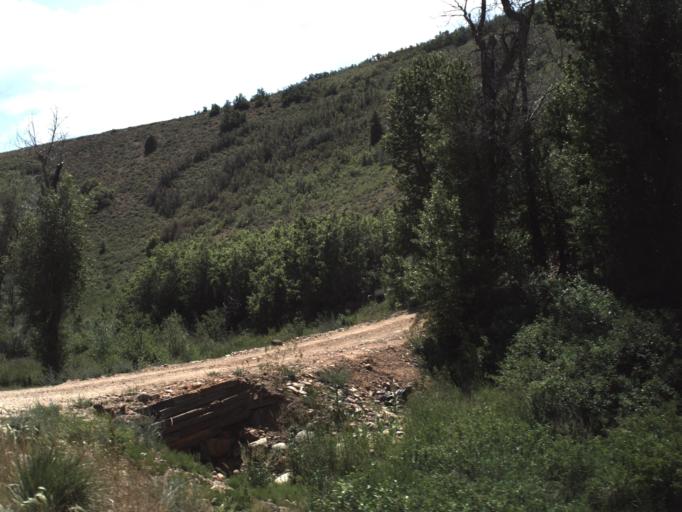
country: US
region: Utah
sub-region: Weber County
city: Wolf Creek
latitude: 41.3669
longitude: -111.5906
